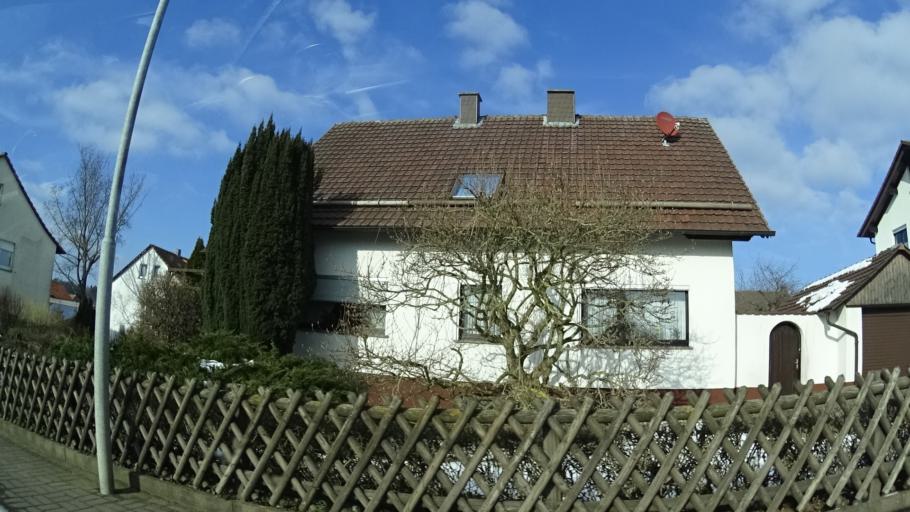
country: DE
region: Thuringia
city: Birx
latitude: 50.5264
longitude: 10.0184
